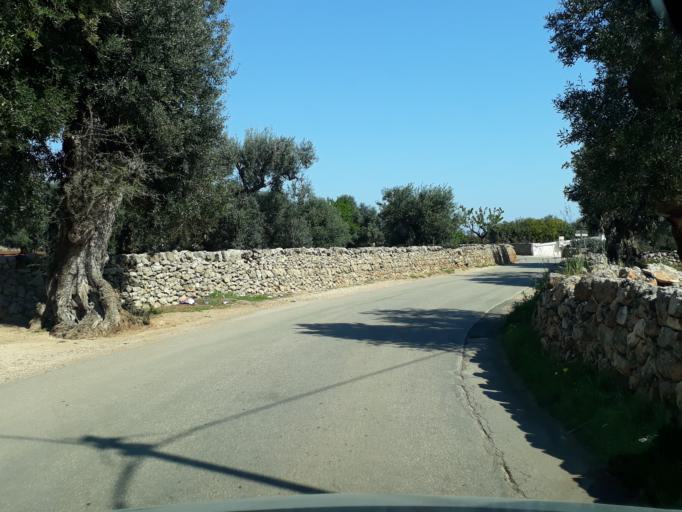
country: IT
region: Apulia
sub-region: Provincia di Brindisi
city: Fasano
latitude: 40.8326
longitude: 17.3779
